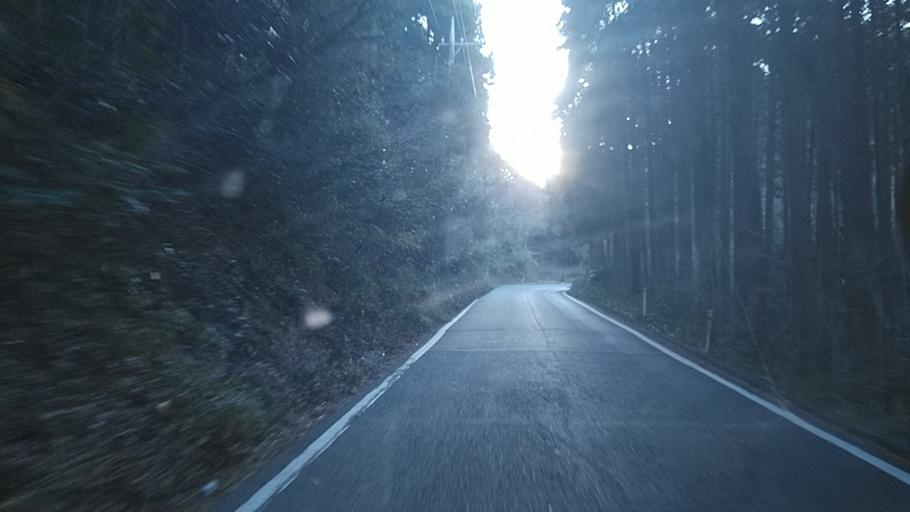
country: JP
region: Chiba
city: Kimitsu
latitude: 35.2572
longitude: 139.9512
